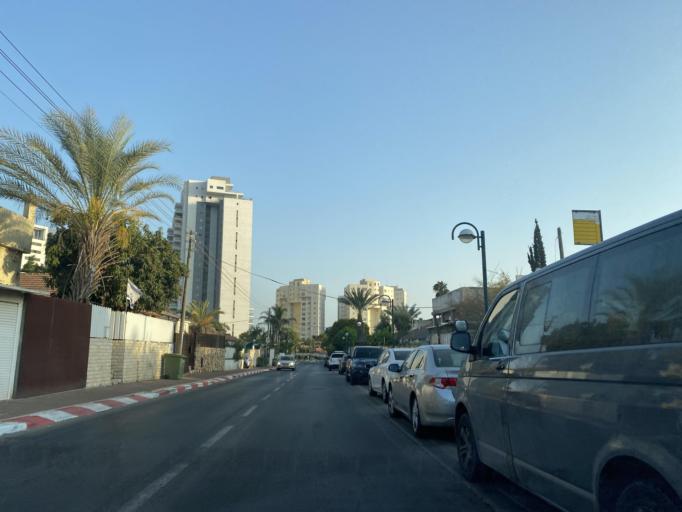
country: IL
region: Tel Aviv
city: Ramat HaSharon
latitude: 32.1338
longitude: 34.8625
